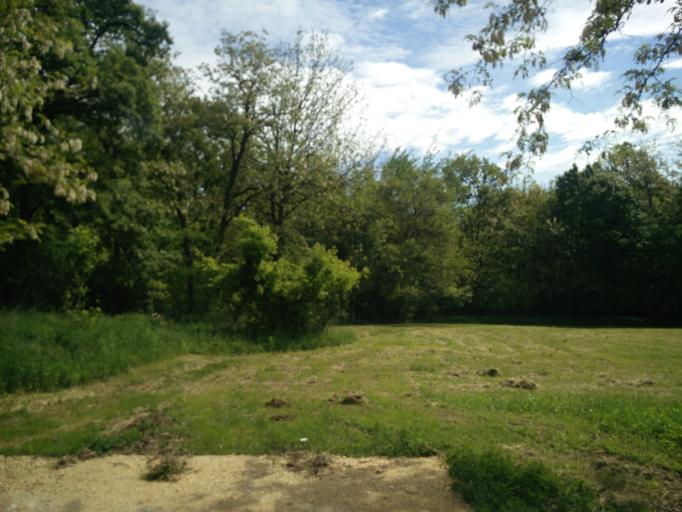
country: HU
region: Tolna
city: Szentgalpuszta
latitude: 46.2844
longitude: 18.6364
